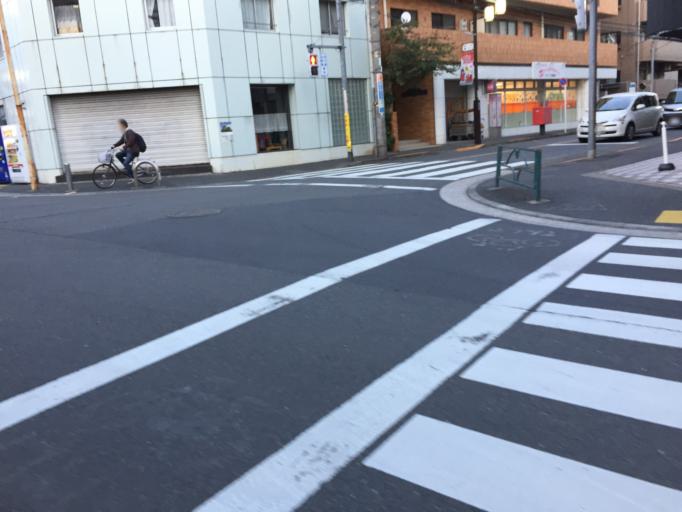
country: JP
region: Tokyo
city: Tokyo
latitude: 35.6357
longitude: 139.6446
